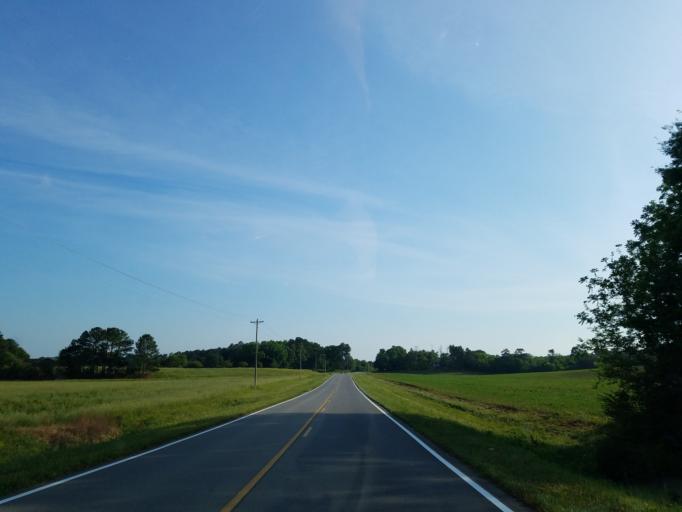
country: US
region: Georgia
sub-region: Chattooga County
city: Trion
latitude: 34.4772
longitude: -85.2623
